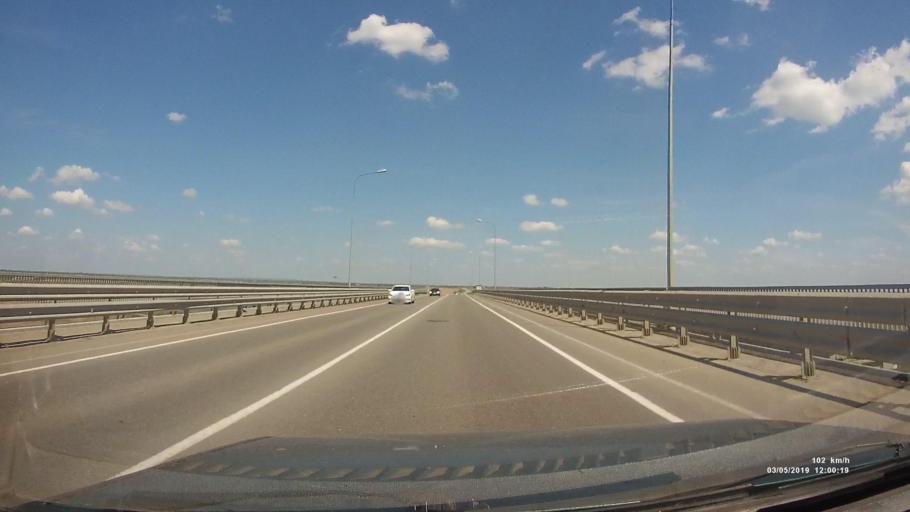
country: RU
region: Rostov
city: Bagayevskaya
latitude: 47.2473
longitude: 40.3391
